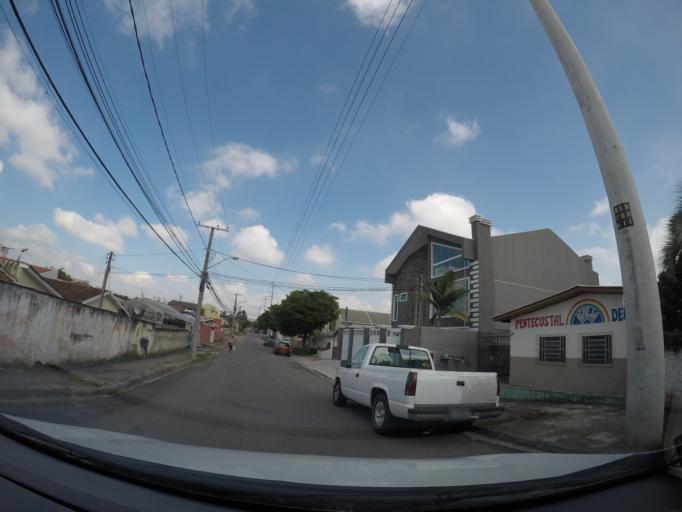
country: BR
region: Parana
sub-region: Sao Jose Dos Pinhais
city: Sao Jose dos Pinhais
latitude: -25.4909
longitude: -49.2263
